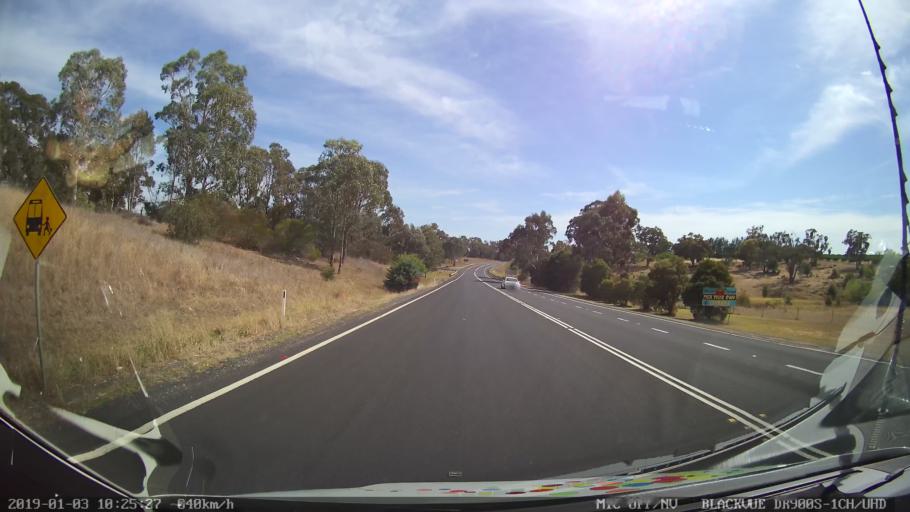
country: AU
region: New South Wales
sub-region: Young
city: Young
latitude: -34.4223
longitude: 148.2441
